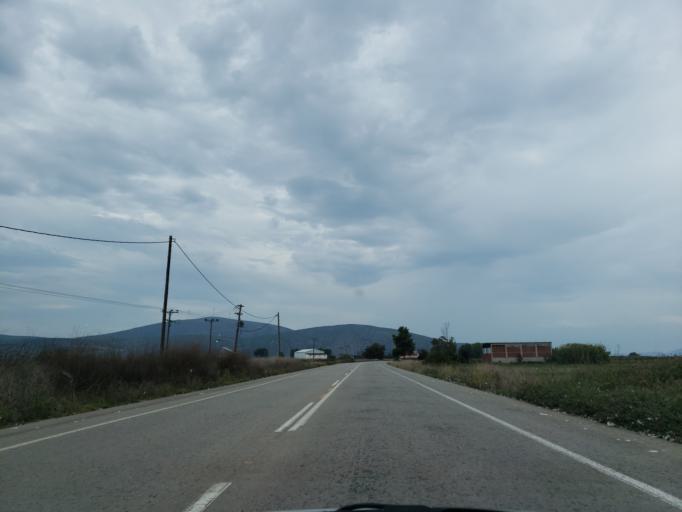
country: GR
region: Central Greece
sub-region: Nomos Voiotias
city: Orchomenos
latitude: 38.4925
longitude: 23.0405
